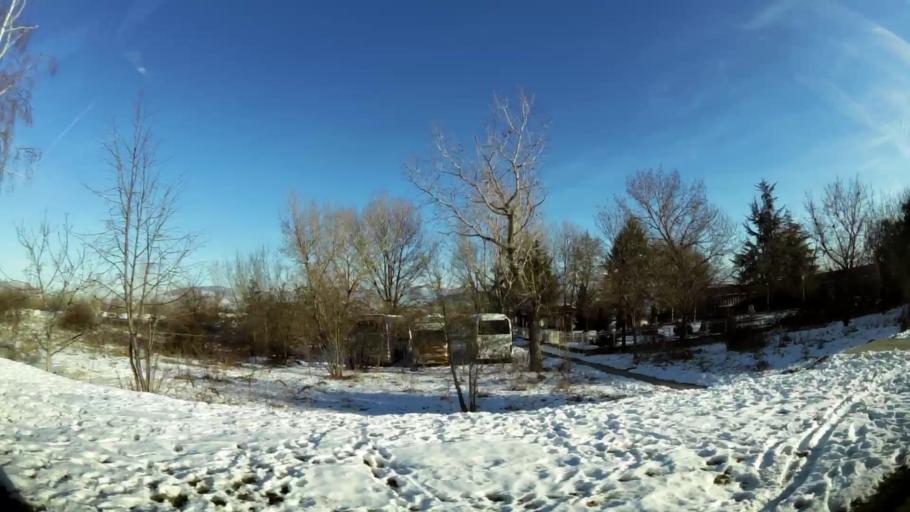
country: MK
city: Krushopek
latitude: 42.0088
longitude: 21.3874
